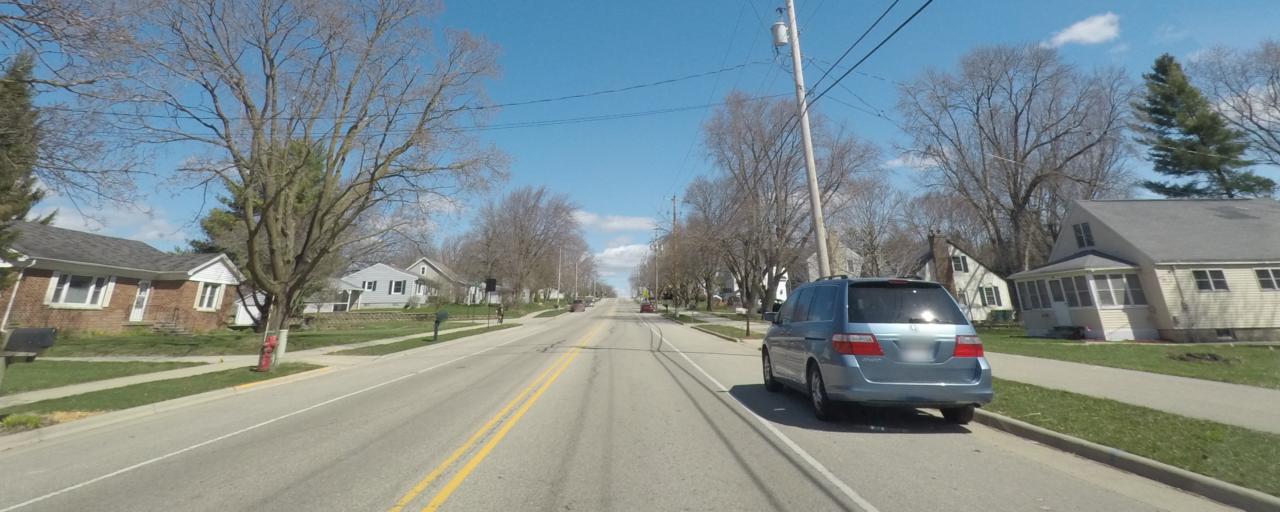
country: US
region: Wisconsin
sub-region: Dane County
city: Cottage Grove
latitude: 43.0807
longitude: -89.1996
